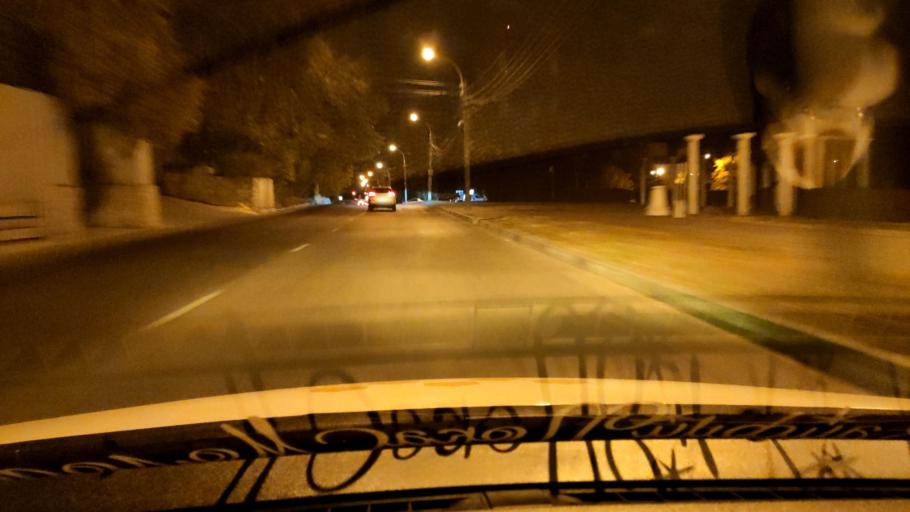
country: RU
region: Voronezj
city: Voronezh
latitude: 51.6580
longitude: 39.2144
